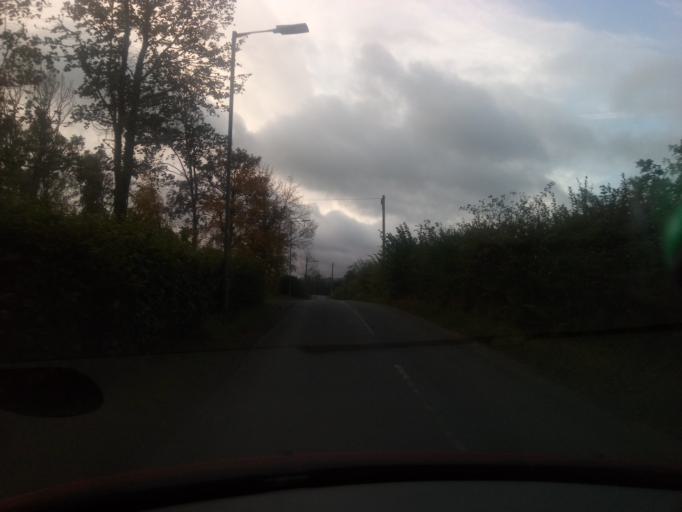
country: GB
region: Scotland
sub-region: The Scottish Borders
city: Jedburgh
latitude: 55.4048
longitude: -2.6552
